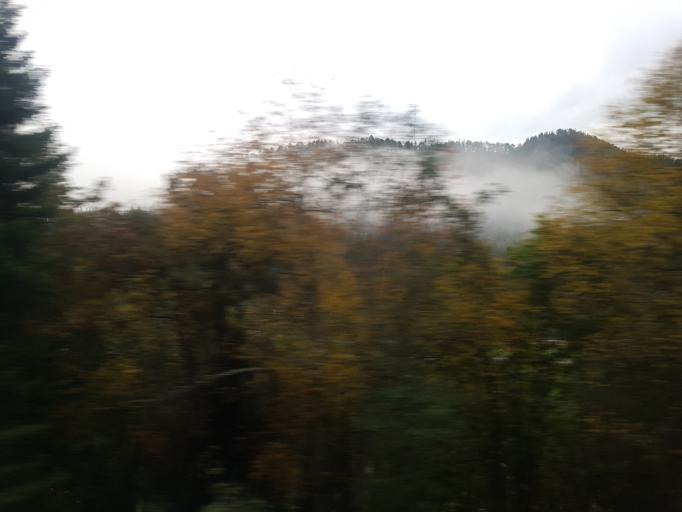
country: NO
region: Sor-Trondelag
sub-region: Midtre Gauldal
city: Storen
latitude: 63.0297
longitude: 10.2650
